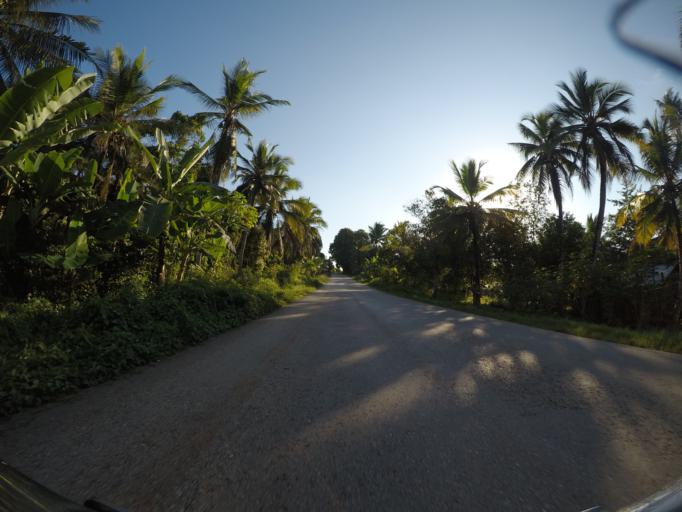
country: TZ
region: Pemba South
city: Mtambile
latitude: -5.3723
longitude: 39.7061
